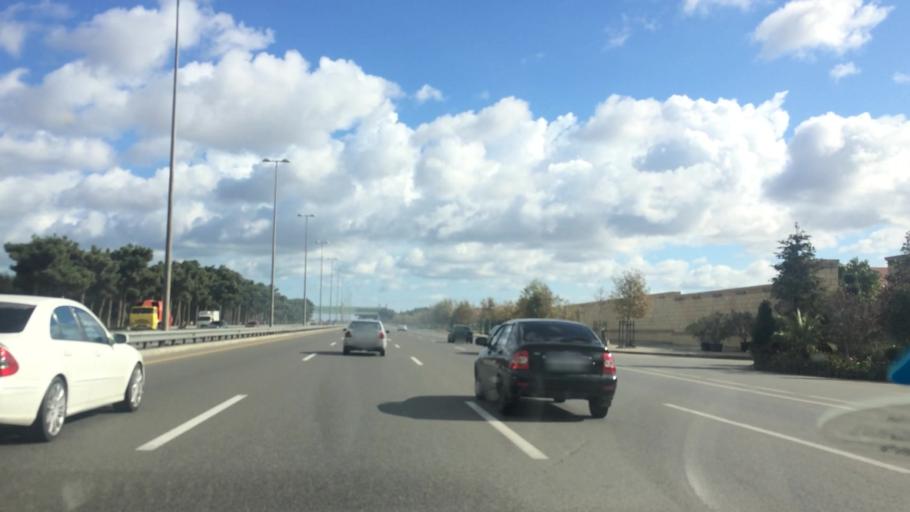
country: AZ
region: Baki
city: Biny Selo
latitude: 40.4646
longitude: 50.0868
